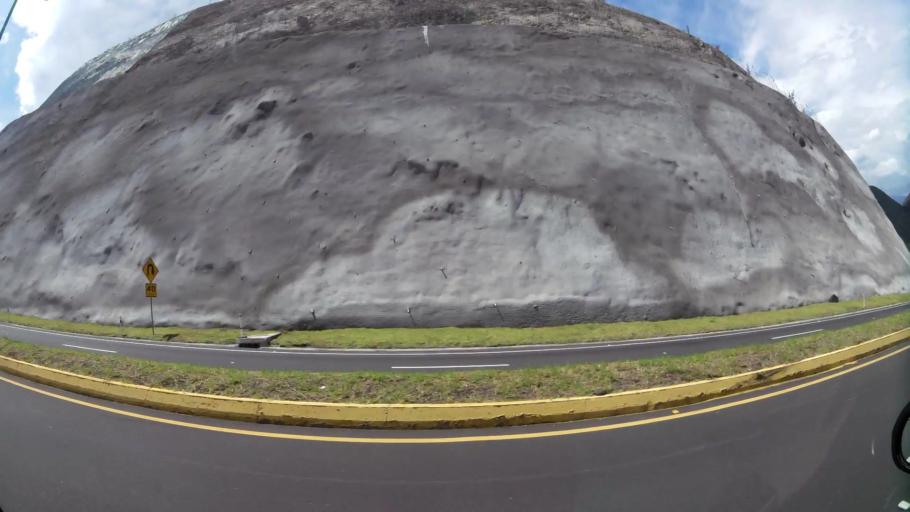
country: EC
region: Pichincha
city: Quito
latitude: -0.1004
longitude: -78.3854
